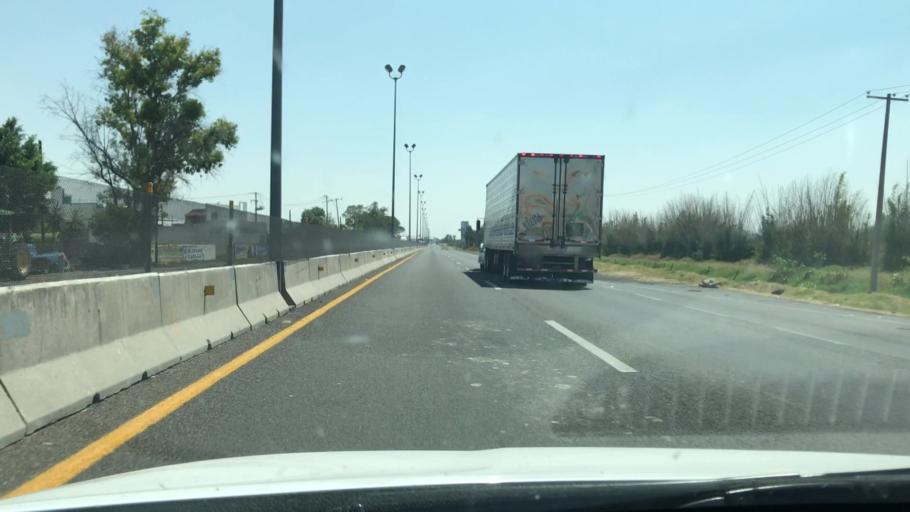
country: MX
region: Guanajuato
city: Abasolo
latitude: 20.4602
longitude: -101.5285
